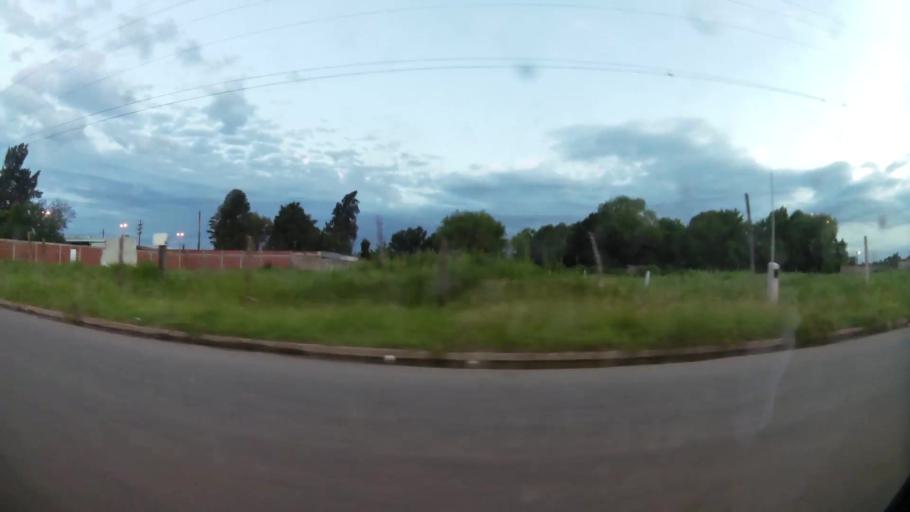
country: AR
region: Buenos Aires
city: San Nicolas de los Arroyos
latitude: -33.3562
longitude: -60.2030
